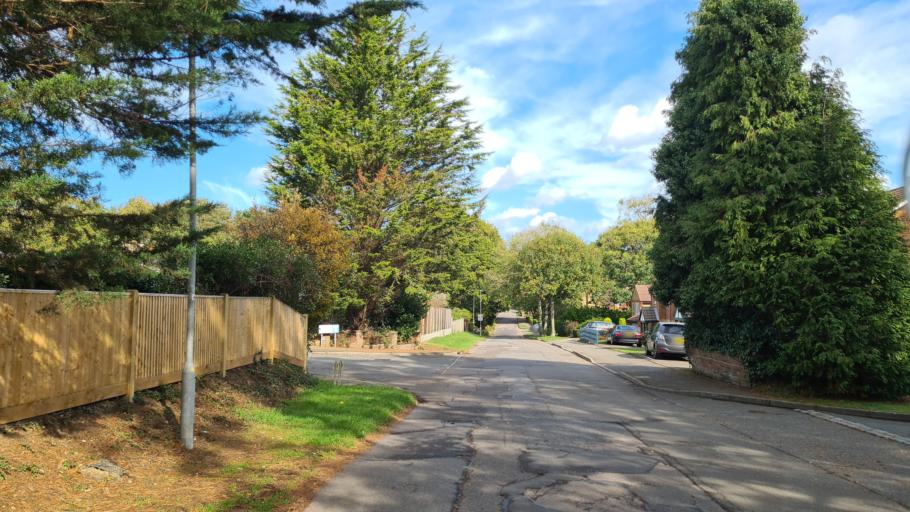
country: GB
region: England
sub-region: East Sussex
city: Hastings
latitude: 50.8778
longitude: 0.5601
